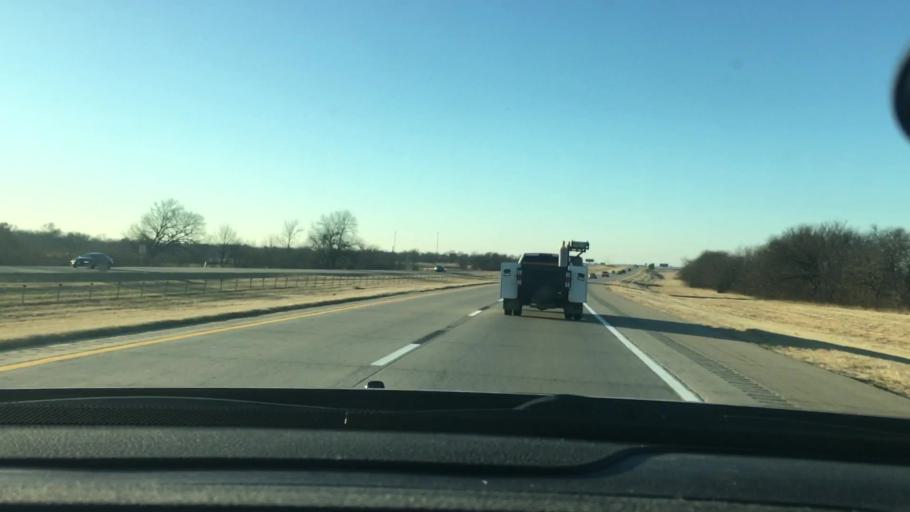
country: US
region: Oklahoma
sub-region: Murray County
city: Davis
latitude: 34.3430
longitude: -97.1482
